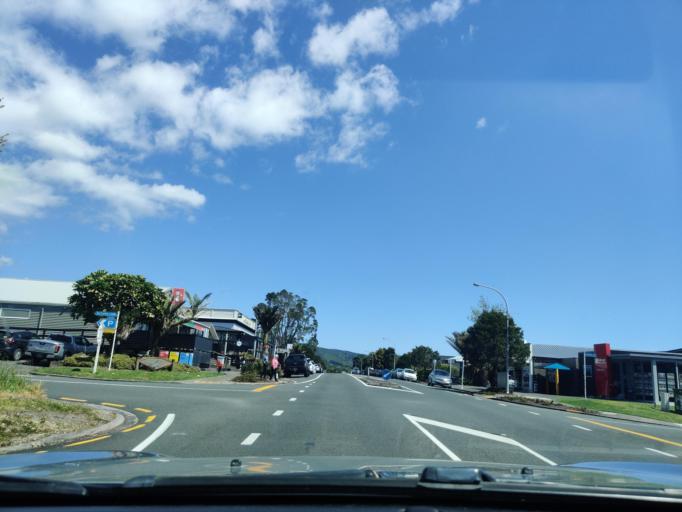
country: NZ
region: Taranaki
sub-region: New Plymouth District
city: New Plymouth
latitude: -39.1151
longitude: 173.9575
